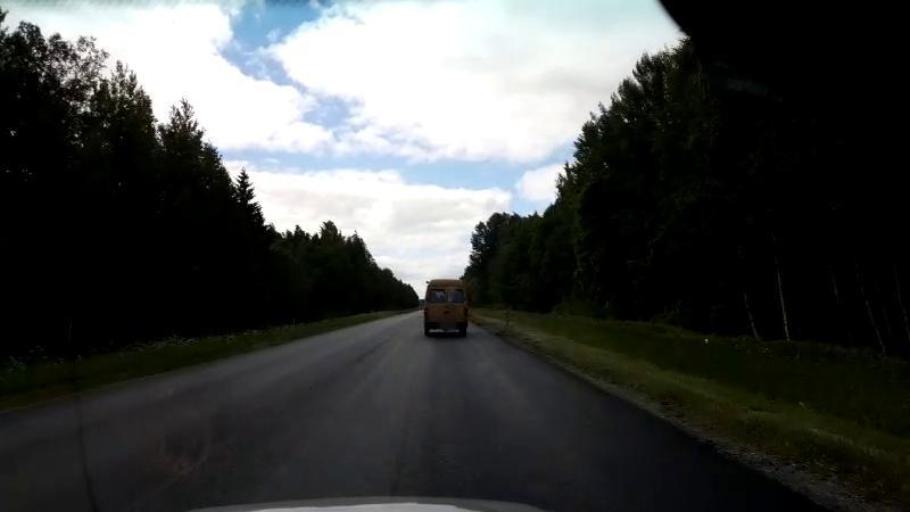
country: LV
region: Salacgrivas
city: Ainazi
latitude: 57.9491
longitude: 24.4361
